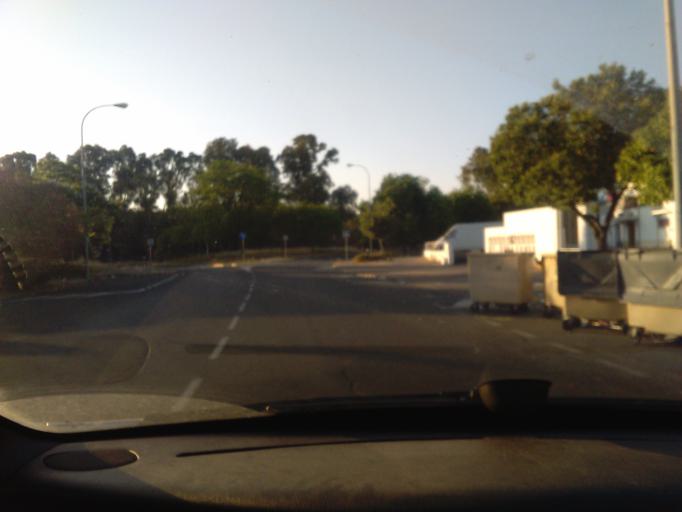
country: ES
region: Andalusia
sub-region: Provincia de Sevilla
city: Sevilla
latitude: 37.3951
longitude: -5.9413
